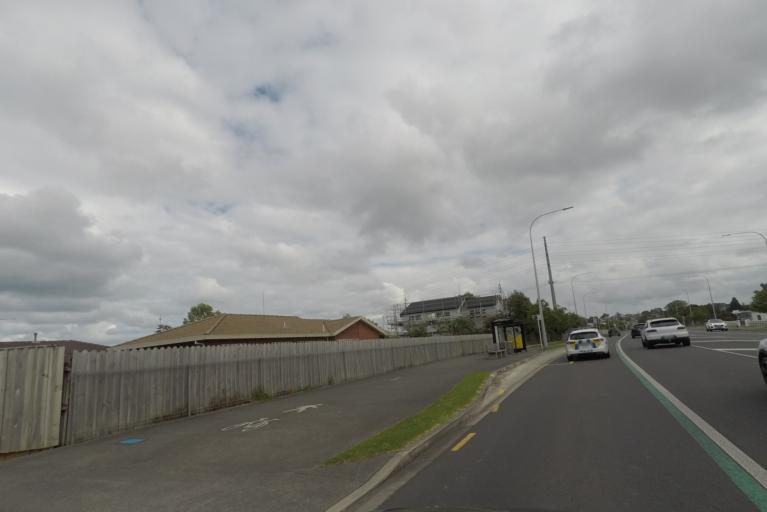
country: NZ
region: Auckland
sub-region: Auckland
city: Rothesay Bay
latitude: -36.7384
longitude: 174.6923
